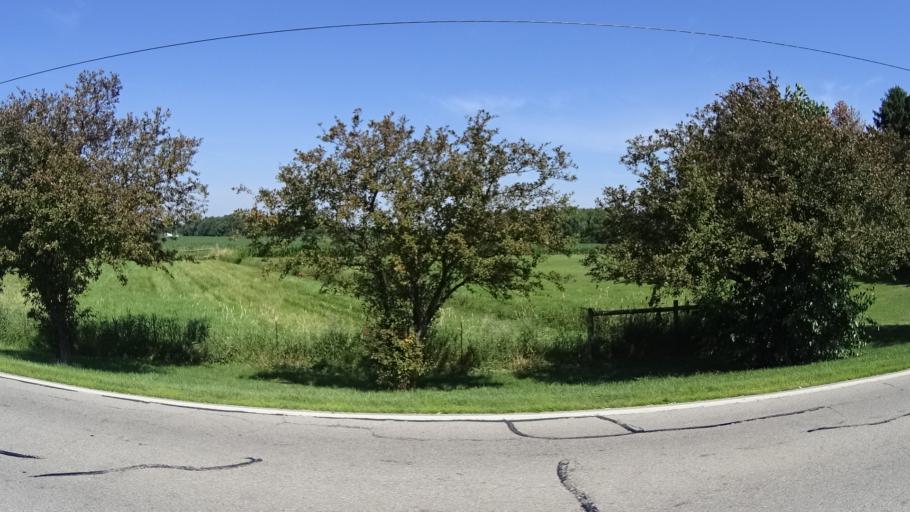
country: US
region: Ohio
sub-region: Huron County
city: Bellevue
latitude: 41.3762
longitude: -82.8415
